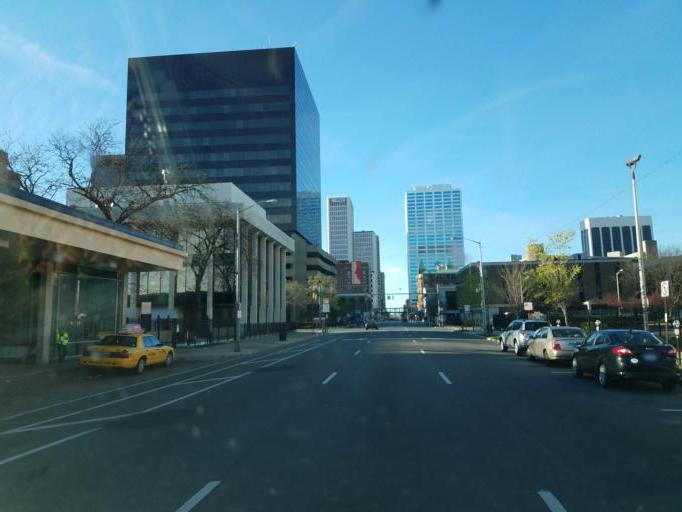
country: US
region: Ohio
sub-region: Franklin County
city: Columbus
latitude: 39.9586
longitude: -82.9955
